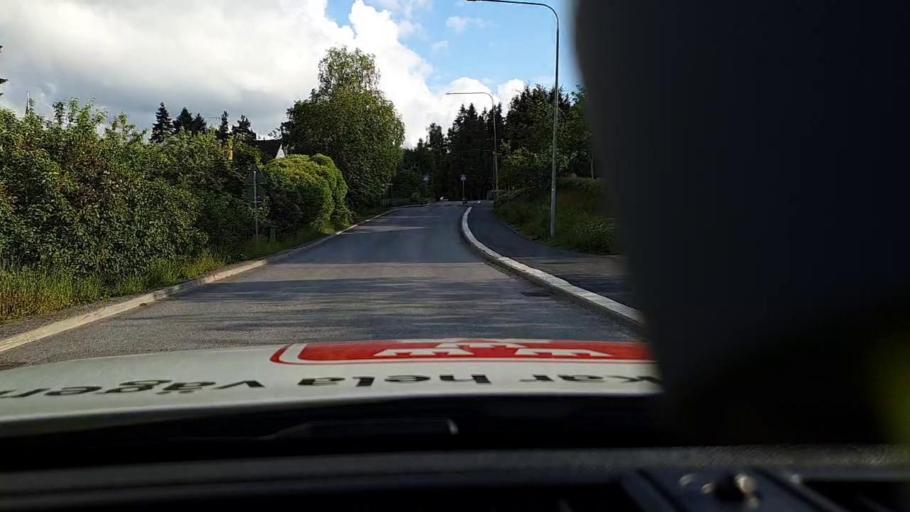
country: SE
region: Stockholm
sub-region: Huddinge Kommun
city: Huddinge
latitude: 59.2497
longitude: 17.9628
